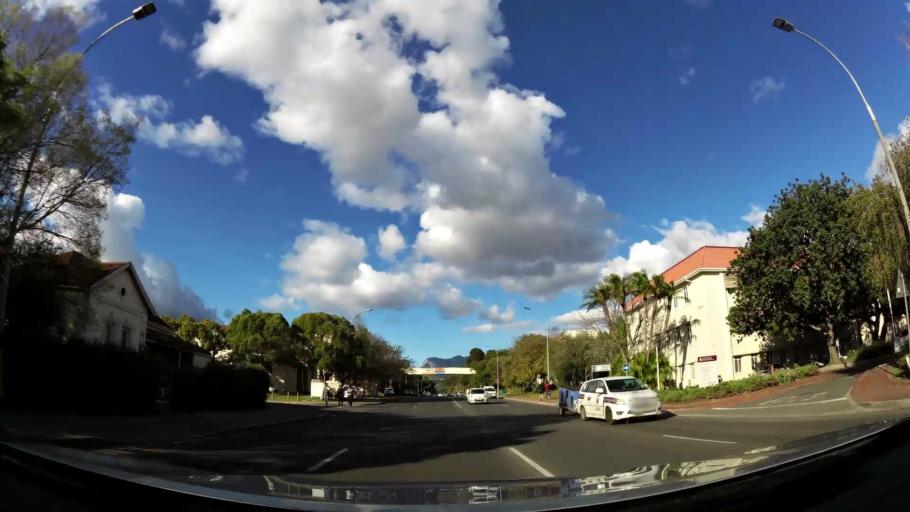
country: ZA
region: Western Cape
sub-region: Cape Winelands District Municipality
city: Stellenbosch
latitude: -33.9316
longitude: 18.8644
